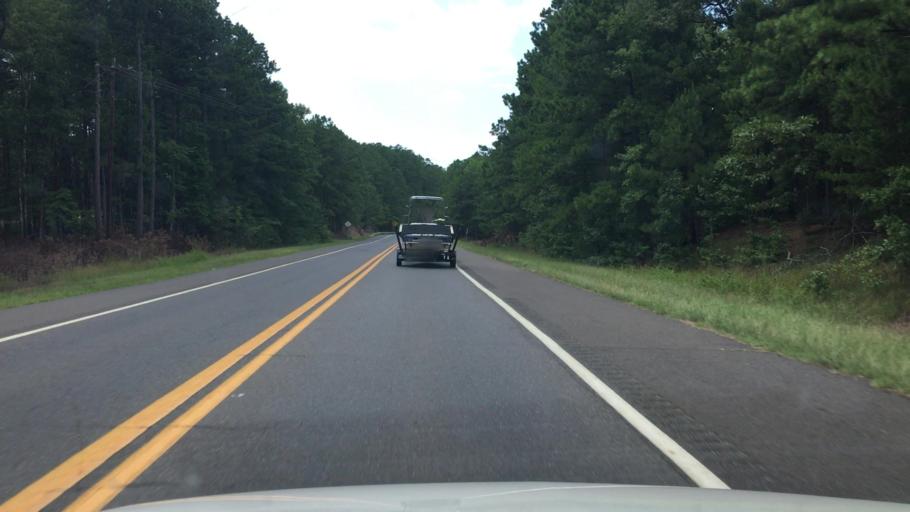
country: US
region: Arkansas
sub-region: Clark County
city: Arkadelphia
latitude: 34.2300
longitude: -93.0945
